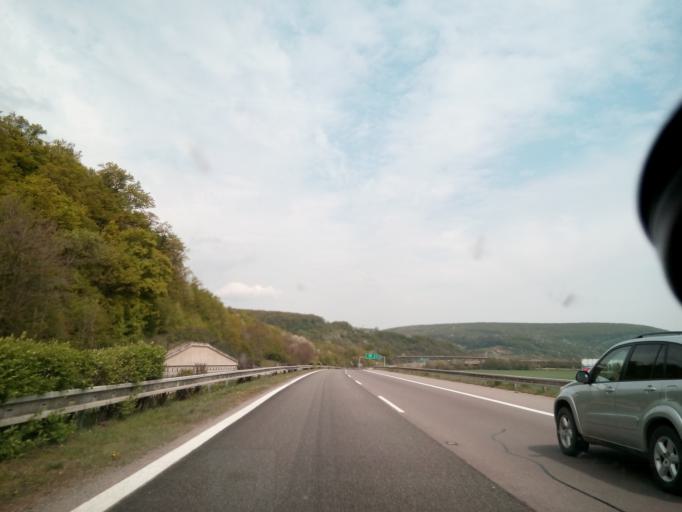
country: SK
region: Trenciansky
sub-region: Okres Trencin
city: Trencin
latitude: 48.8980
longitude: 17.9842
